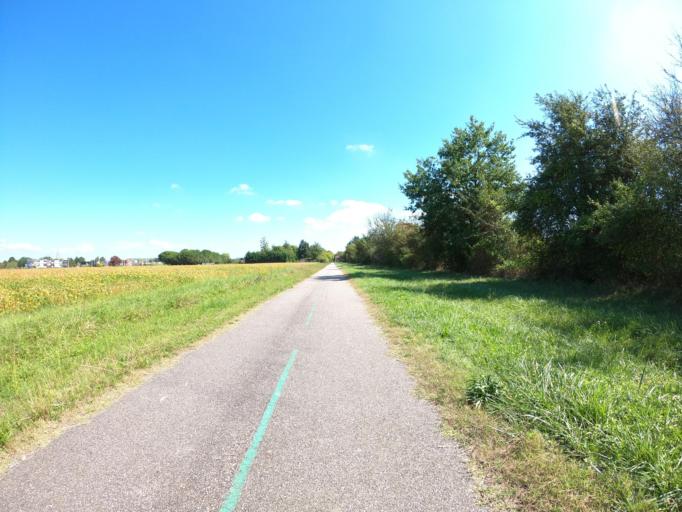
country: FR
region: Aquitaine
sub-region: Departement du Lot-et-Garonne
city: Bias
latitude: 44.4011
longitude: 0.6675
